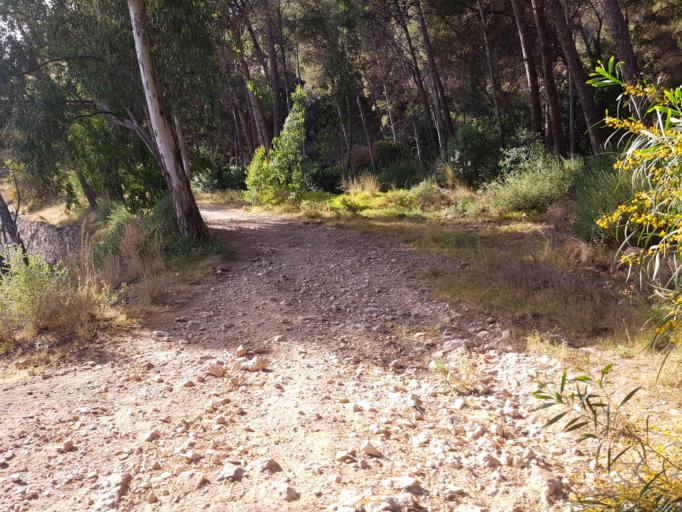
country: ES
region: Andalusia
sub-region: Provincia de Malaga
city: Marbella
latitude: 36.5296
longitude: -4.8824
